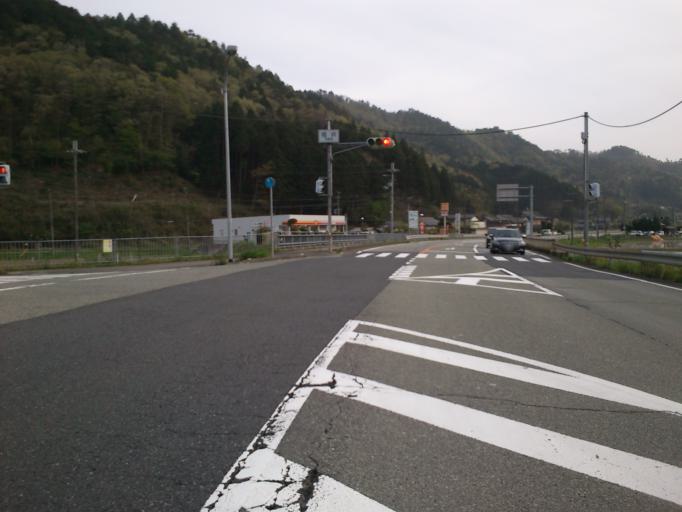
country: JP
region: Hyogo
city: Sasayama
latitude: 35.1177
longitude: 135.3366
